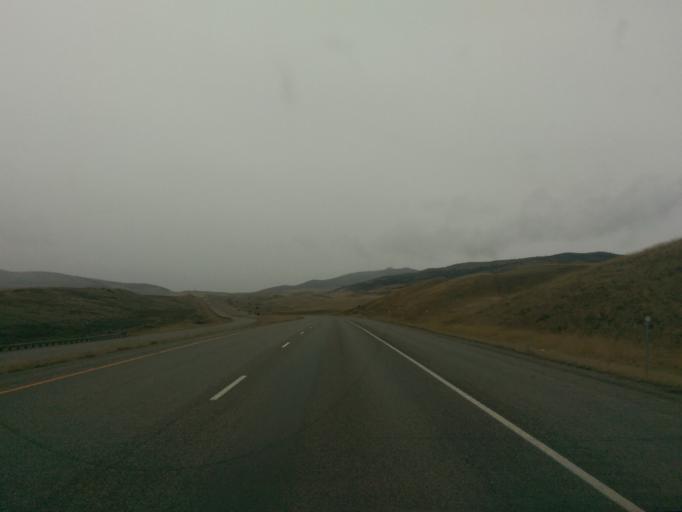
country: US
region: Montana
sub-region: Gallatin County
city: Three Forks
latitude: 45.9098
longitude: -111.7870
